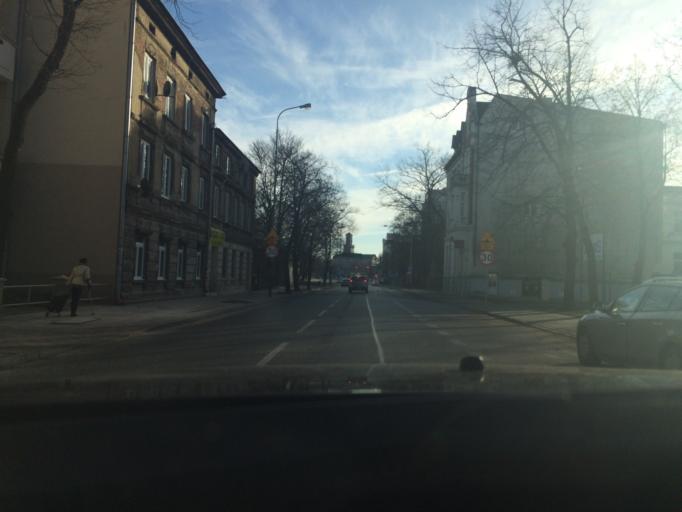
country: PL
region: Lodz Voivodeship
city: Lodz
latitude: 51.7624
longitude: 19.4403
